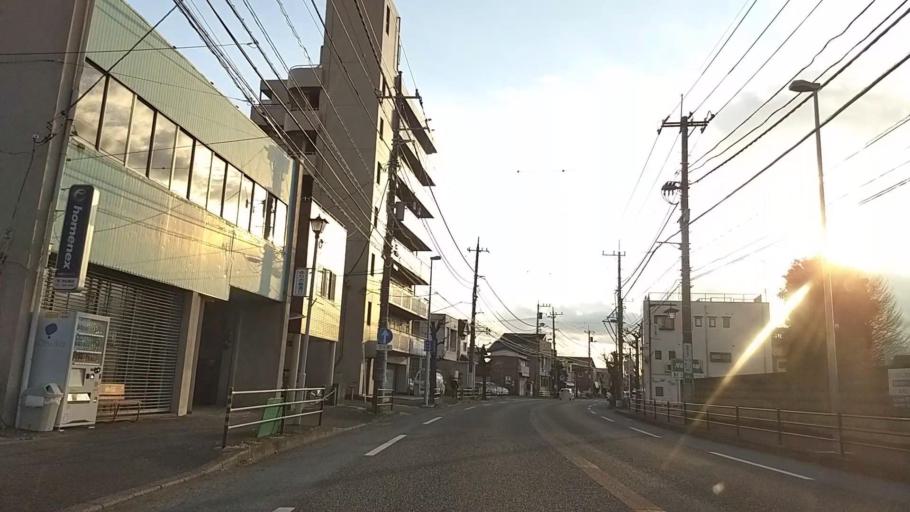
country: JP
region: Kanagawa
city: Atsugi
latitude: 35.4375
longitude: 139.3702
